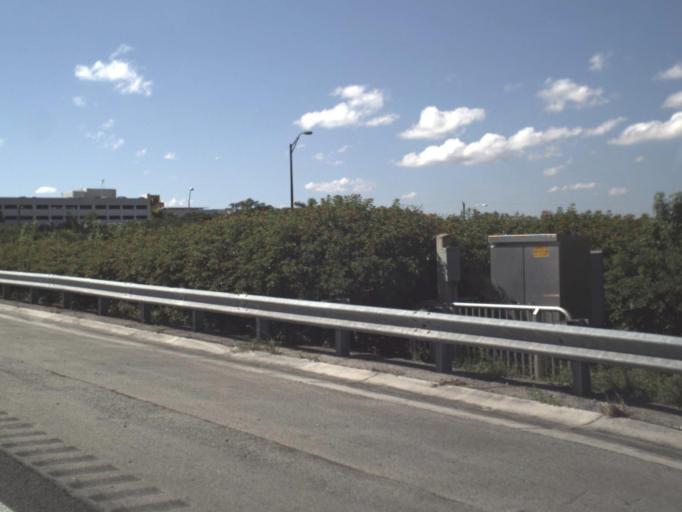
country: US
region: Florida
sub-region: Miami-Dade County
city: Westwood Lake
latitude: 25.7343
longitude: -80.3845
